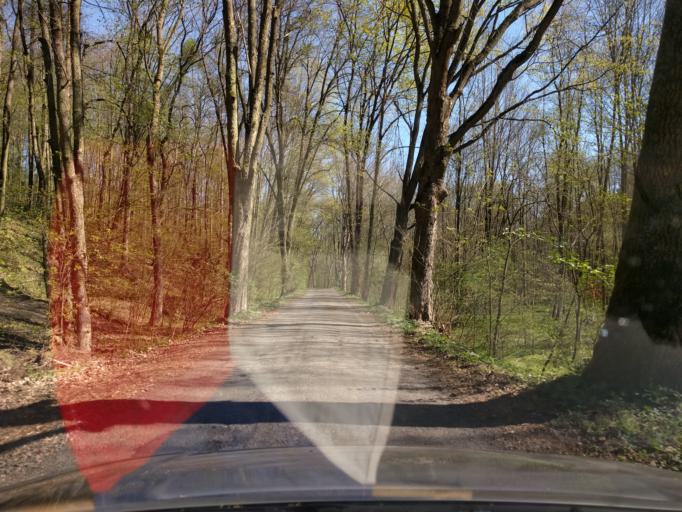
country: CZ
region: Central Bohemia
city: Cesky Brod
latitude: 50.0388
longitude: 14.8358
